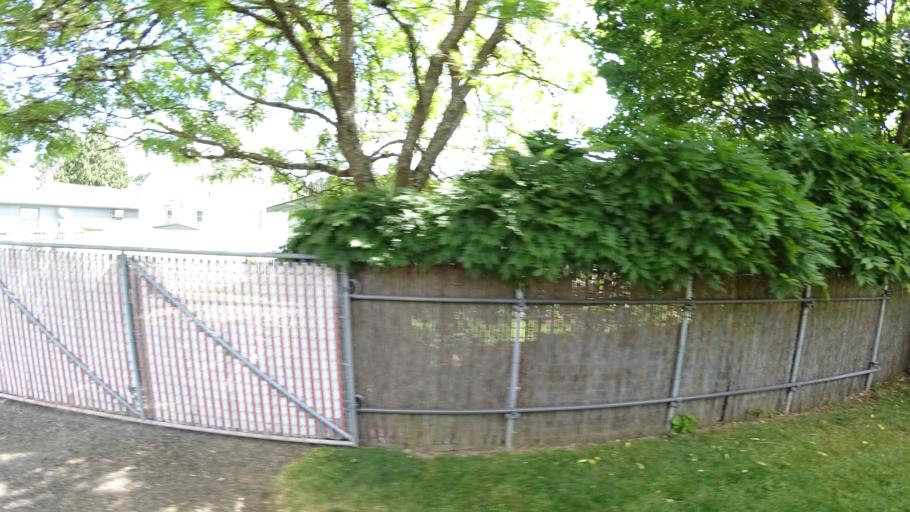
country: US
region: Oregon
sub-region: Washington County
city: West Haven
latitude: 45.5981
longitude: -122.7594
